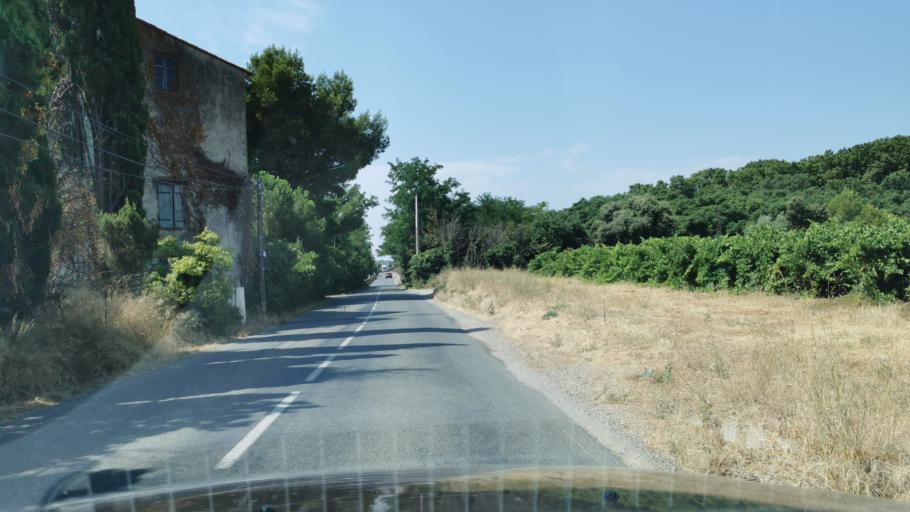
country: FR
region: Languedoc-Roussillon
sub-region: Departement de l'Aude
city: Argeliers
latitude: 43.2854
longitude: 2.9022
